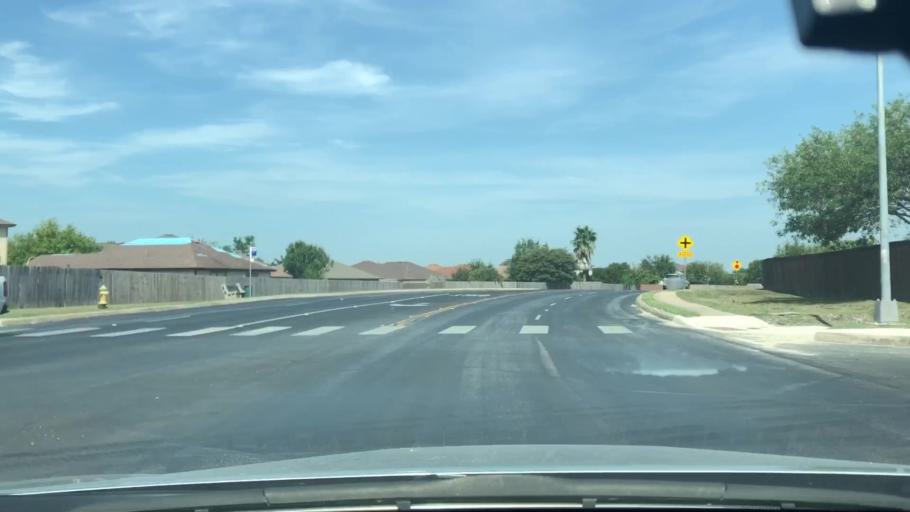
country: US
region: Texas
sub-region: Bexar County
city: Converse
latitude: 29.4902
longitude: -98.3121
